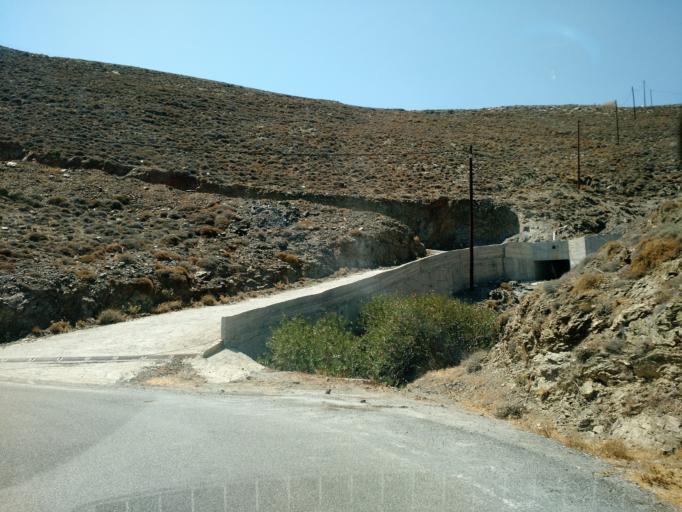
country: GR
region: South Aegean
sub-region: Nomos Dodekanisou
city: Astypalaia
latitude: 36.5511
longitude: 26.3495
